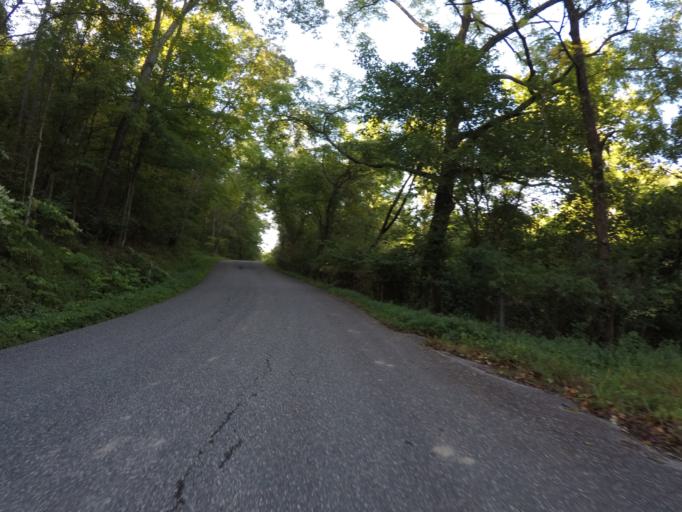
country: US
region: Ohio
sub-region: Lawrence County
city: Coal Grove
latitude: 38.5330
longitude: -82.5335
